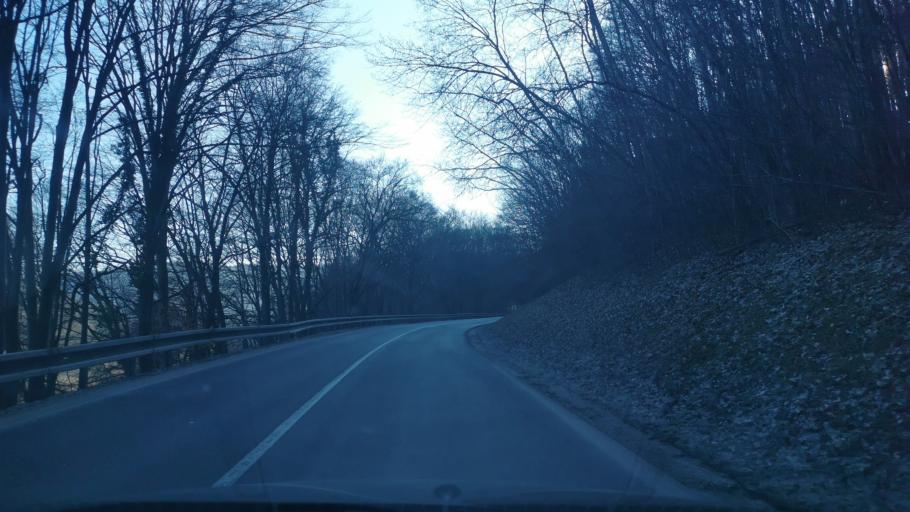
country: SK
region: Trenciansky
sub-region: Okres Myjava
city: Myjava
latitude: 48.7494
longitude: 17.4874
